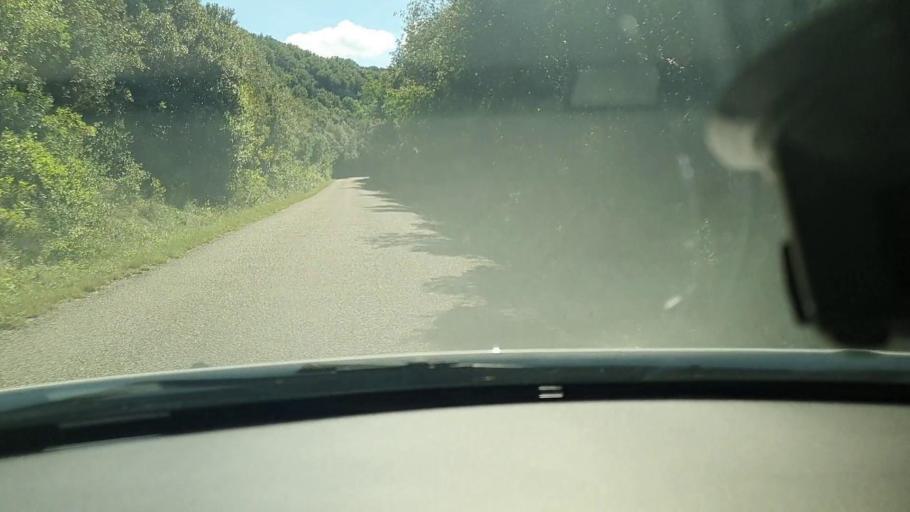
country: FR
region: Languedoc-Roussillon
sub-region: Departement du Gard
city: Goudargues
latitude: 44.1637
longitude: 4.4326
